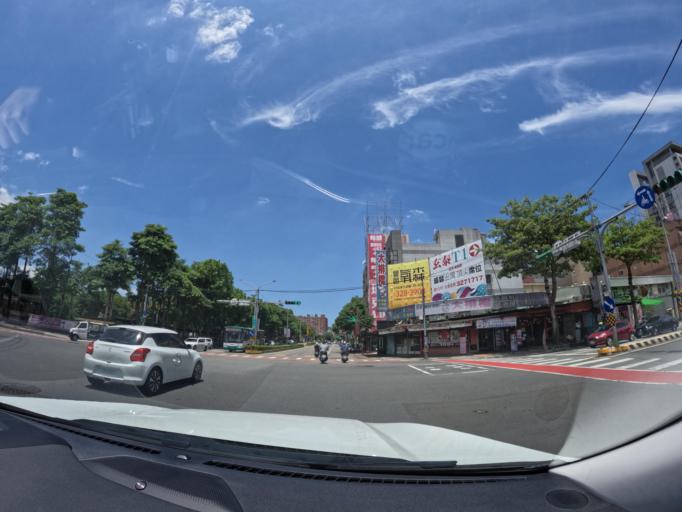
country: TW
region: Taiwan
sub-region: Taoyuan
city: Taoyuan
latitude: 25.0515
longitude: 121.3726
